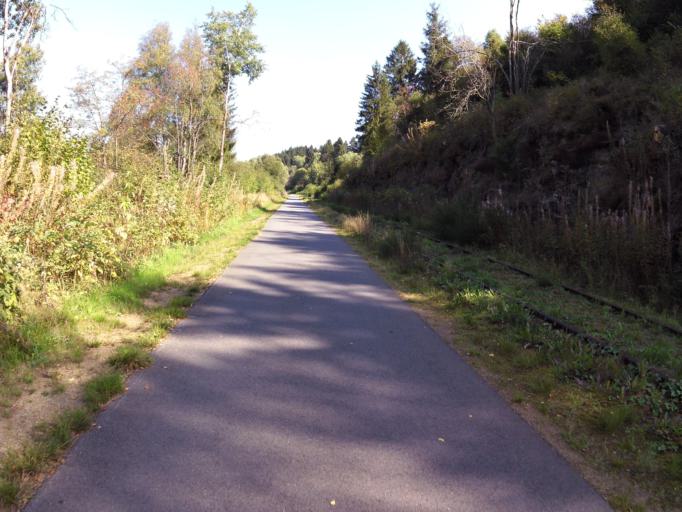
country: DE
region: North Rhine-Westphalia
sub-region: Regierungsbezirk Koln
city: Monschau
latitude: 50.5139
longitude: 6.1992
